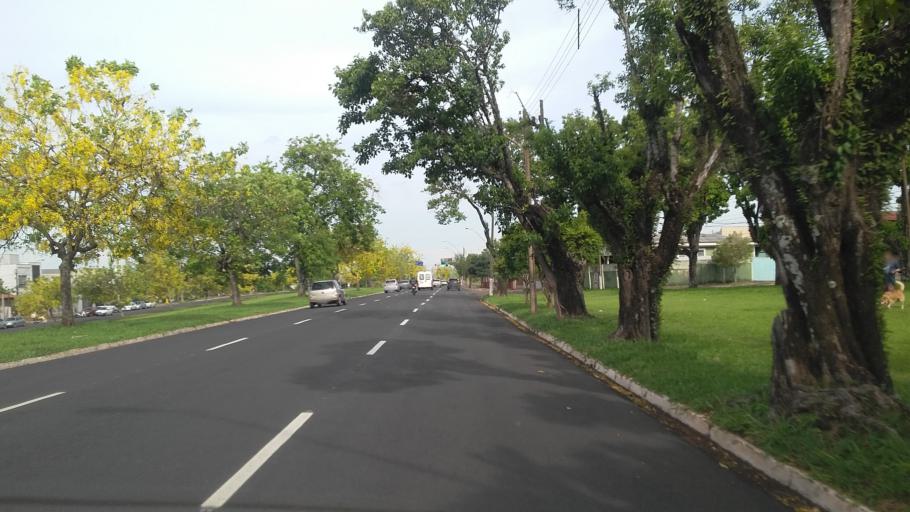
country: BR
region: Parana
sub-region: Londrina
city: Londrina
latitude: -23.2975
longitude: -51.1844
